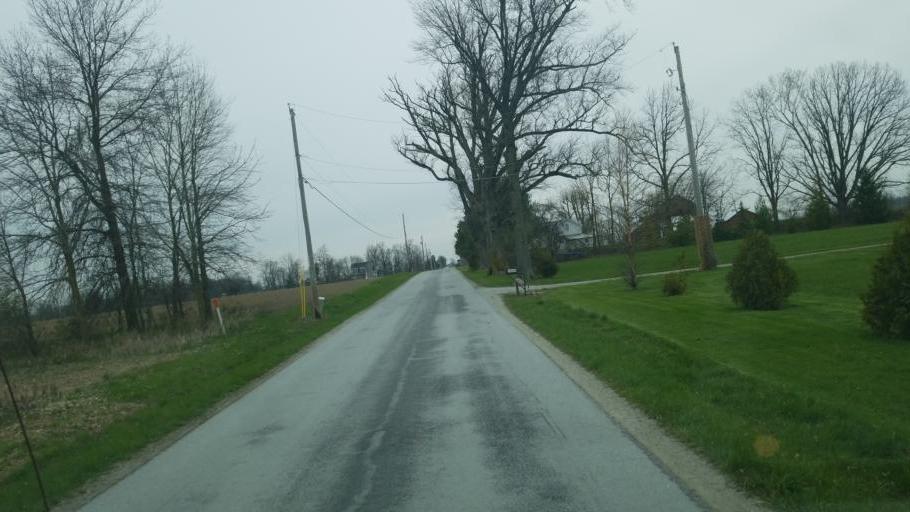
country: US
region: Ohio
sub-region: Hardin County
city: Forest
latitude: 40.8178
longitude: -83.4813
